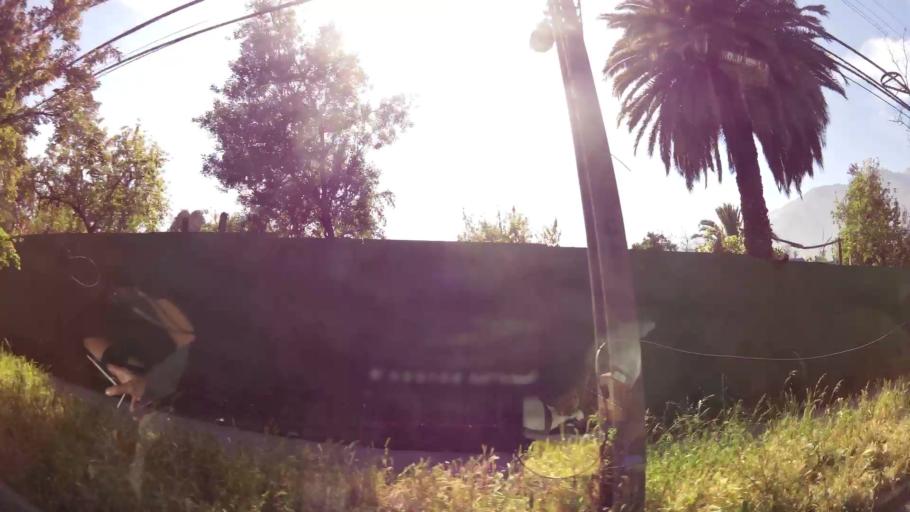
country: CL
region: Santiago Metropolitan
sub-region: Provincia de Santiago
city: Villa Presidente Frei, Nunoa, Santiago, Chile
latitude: -33.4442
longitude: -70.5318
